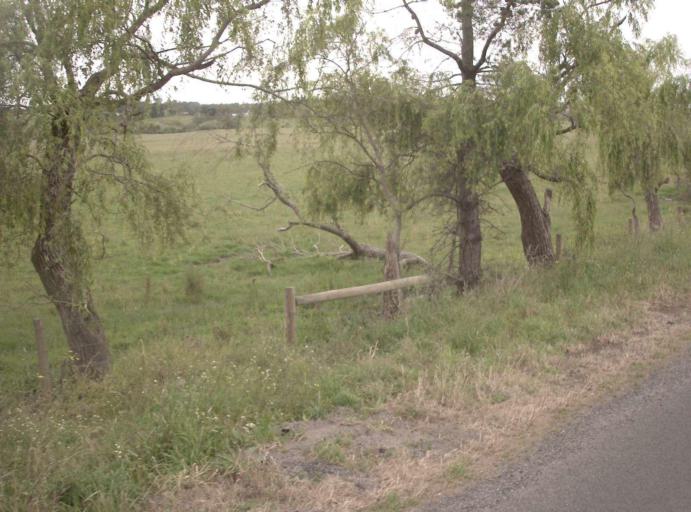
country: AU
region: Victoria
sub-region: Baw Baw
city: Warragul
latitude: -38.5082
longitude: 145.9519
